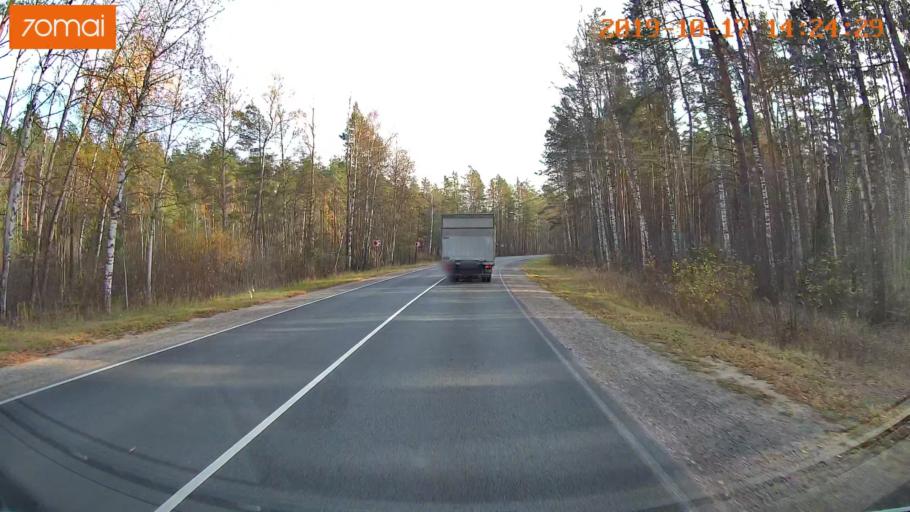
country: RU
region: Moskovskaya
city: Radovitskiy
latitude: 55.0090
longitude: 39.9687
